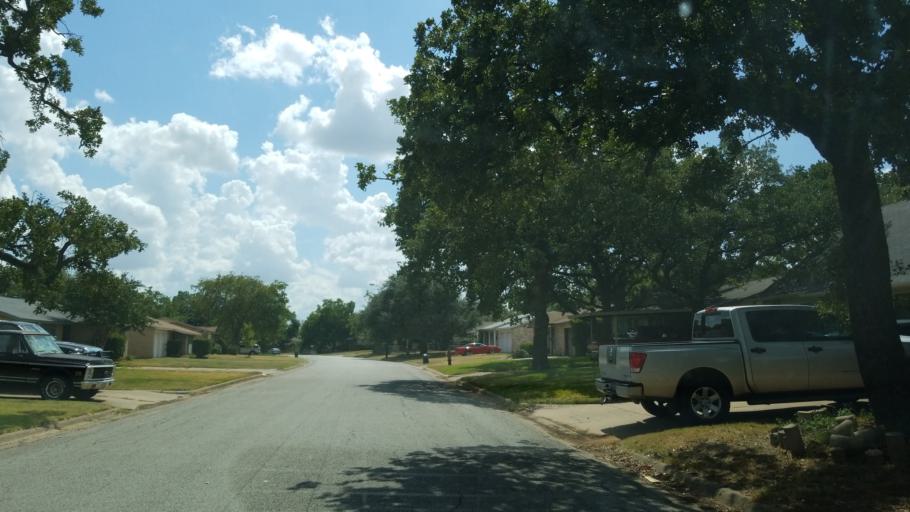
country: US
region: Texas
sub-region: Tarrant County
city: Euless
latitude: 32.8540
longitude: -97.0941
